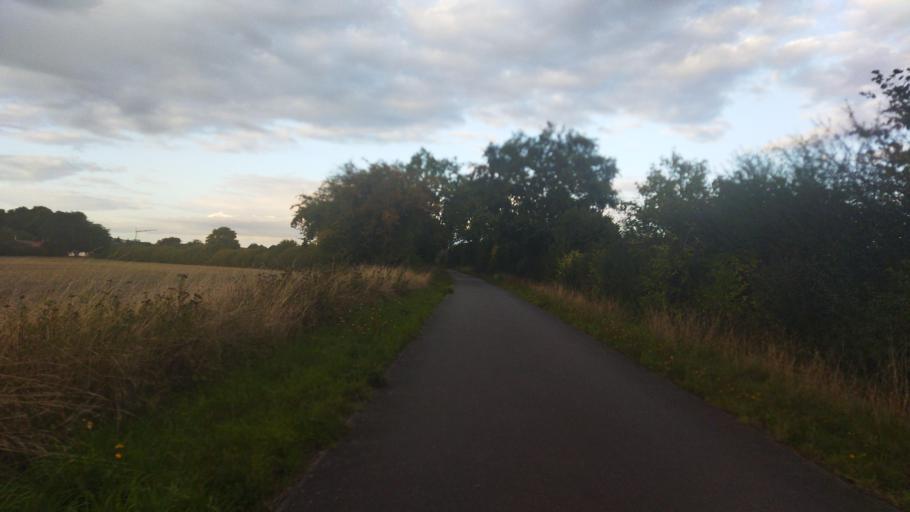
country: DE
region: North Rhine-Westphalia
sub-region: Regierungsbezirk Munster
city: Billerbeck
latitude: 52.0155
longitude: 7.2707
